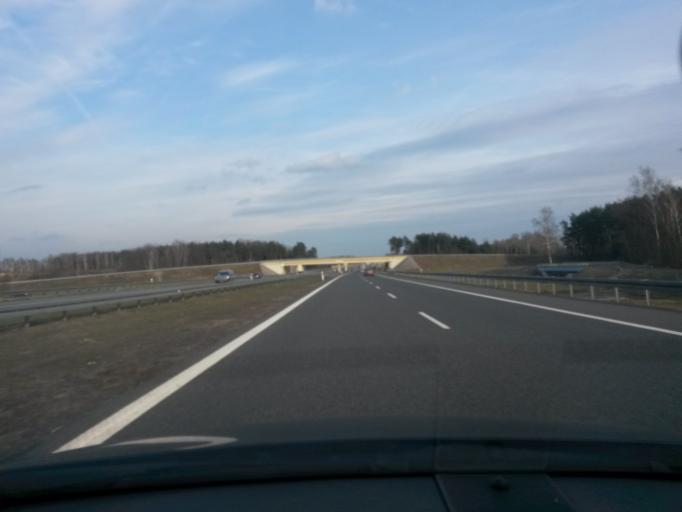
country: PL
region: Lodz Voivodeship
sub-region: Powiat zgierski
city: Ozorkow
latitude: 51.9356
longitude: 19.2630
